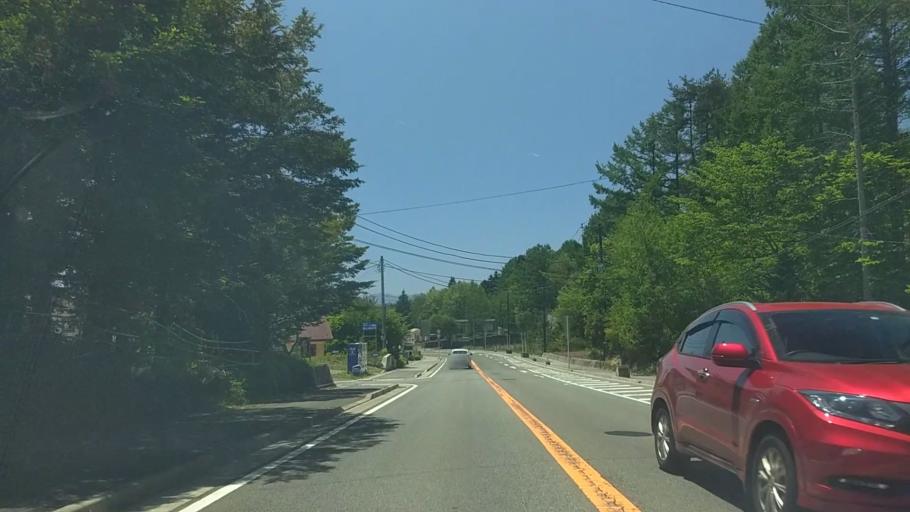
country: JP
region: Yamanashi
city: Nirasaki
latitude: 35.9046
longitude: 138.4437
